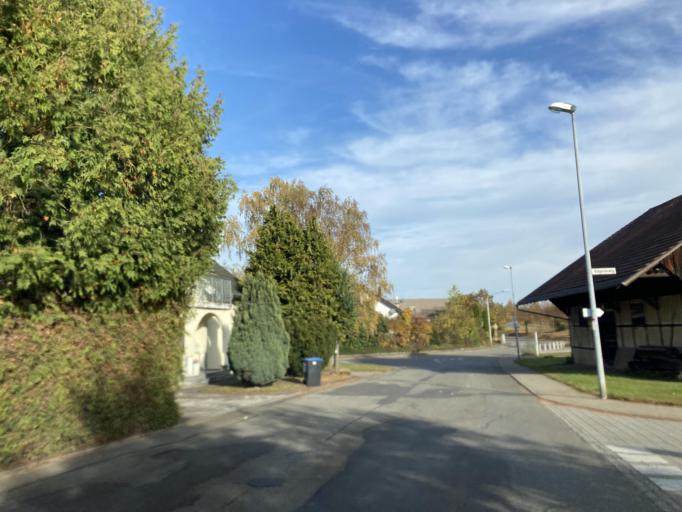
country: DE
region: Baden-Wuerttemberg
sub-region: Tuebingen Region
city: Bodelshausen
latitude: 48.3975
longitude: 8.9766
